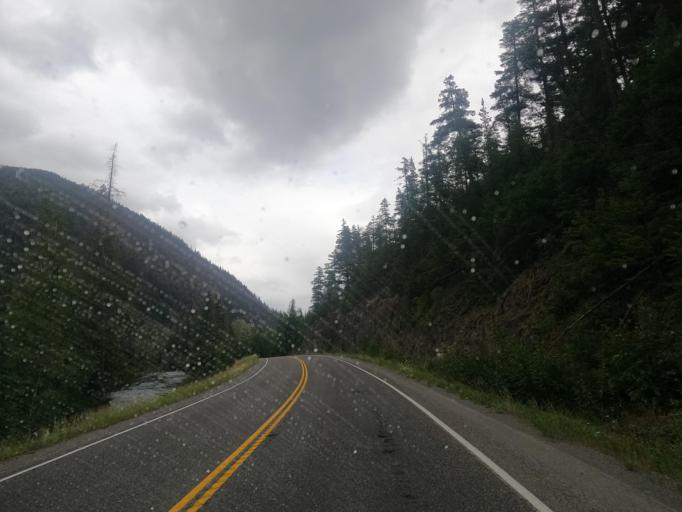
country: CA
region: British Columbia
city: Lillooet
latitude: 50.4880
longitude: -122.2038
